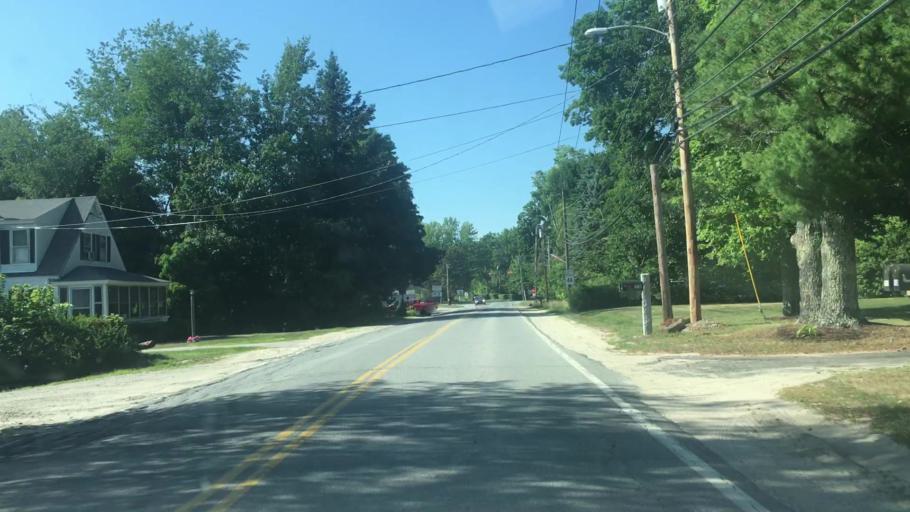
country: US
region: Maine
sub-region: York County
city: Buxton
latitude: 43.6109
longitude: -70.5404
